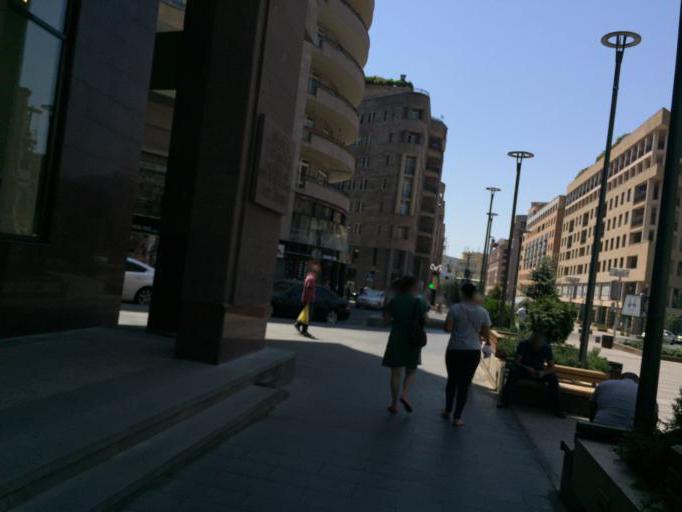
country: AM
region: Yerevan
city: Yerevan
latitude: 40.1834
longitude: 44.5149
